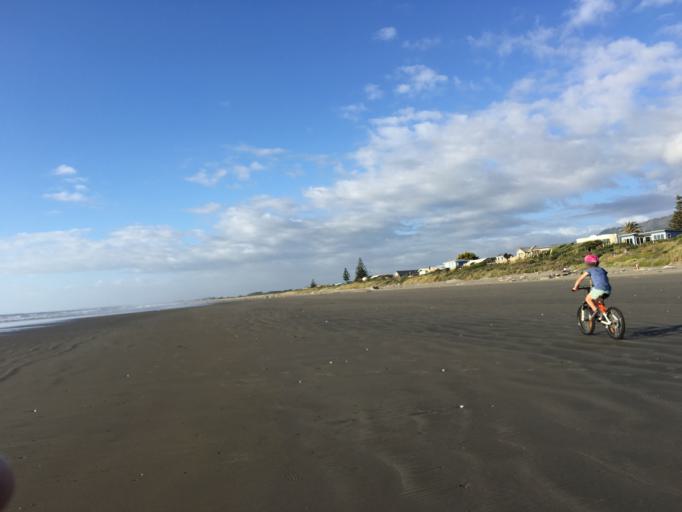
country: NZ
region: Wellington
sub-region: Kapiti Coast District
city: Paraparaumu
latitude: -40.8553
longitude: 175.0298
